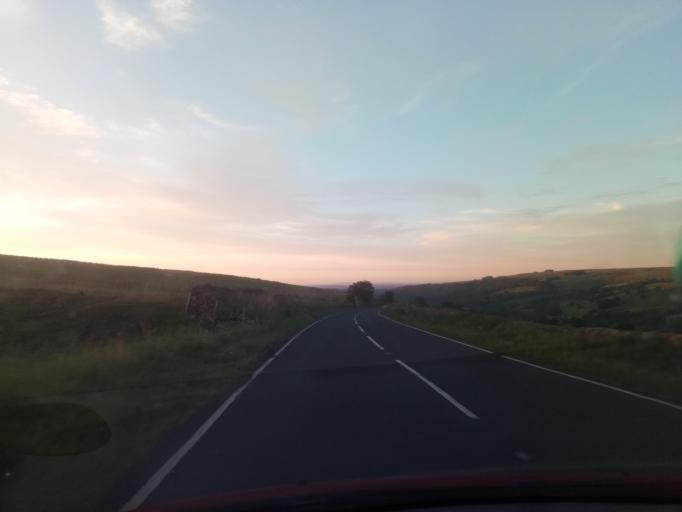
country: GB
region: England
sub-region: Northumberland
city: Bardon Mill
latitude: 54.8674
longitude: -2.3567
